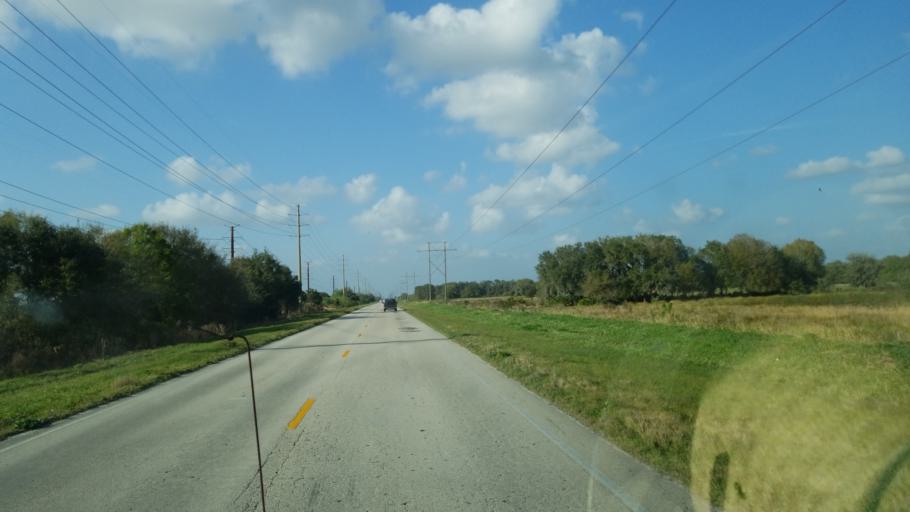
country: US
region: Florida
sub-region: Hardee County
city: Wauchula
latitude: 27.5361
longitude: -81.9290
